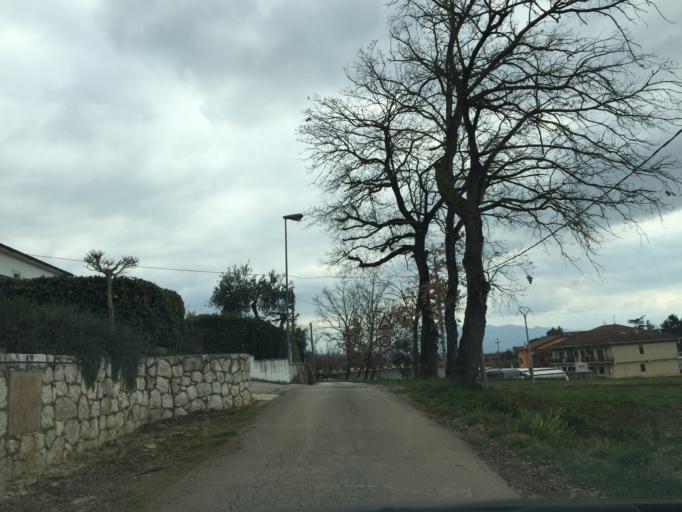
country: IT
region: Latium
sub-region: Provincia di Frosinone
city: Cassino
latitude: 41.4830
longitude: 13.8015
